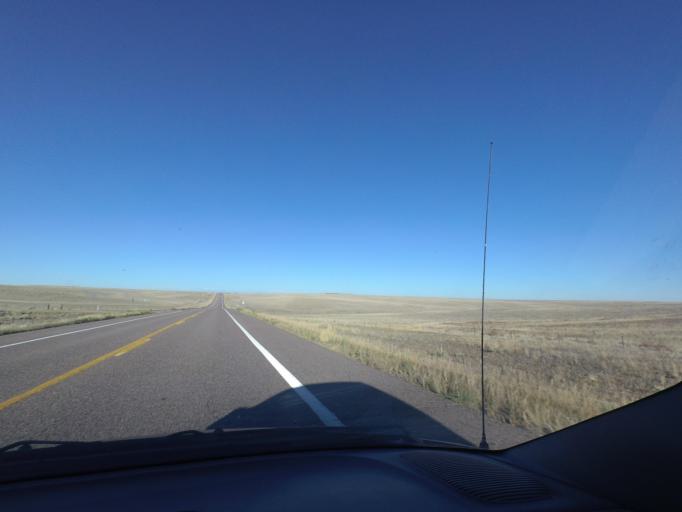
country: US
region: Colorado
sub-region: Arapahoe County
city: Byers
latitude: 39.7329
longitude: -103.9260
